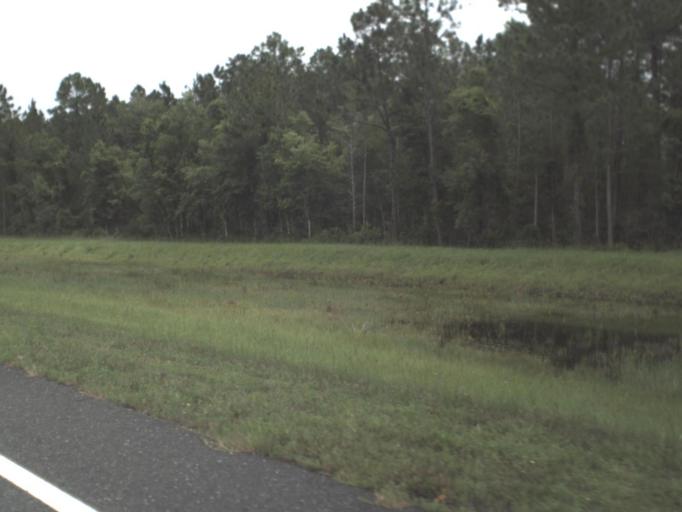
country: US
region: Florida
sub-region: Levy County
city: Chiefland
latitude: 29.3696
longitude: -82.7942
